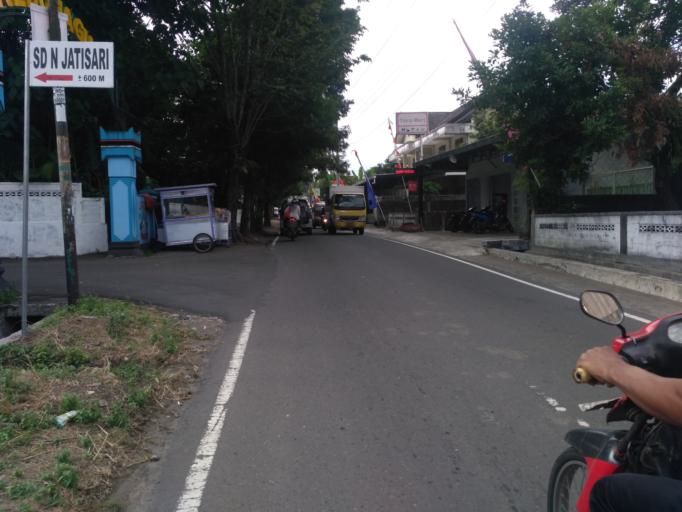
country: ID
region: Daerah Istimewa Yogyakarta
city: Sleman
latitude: -7.7261
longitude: 110.3568
